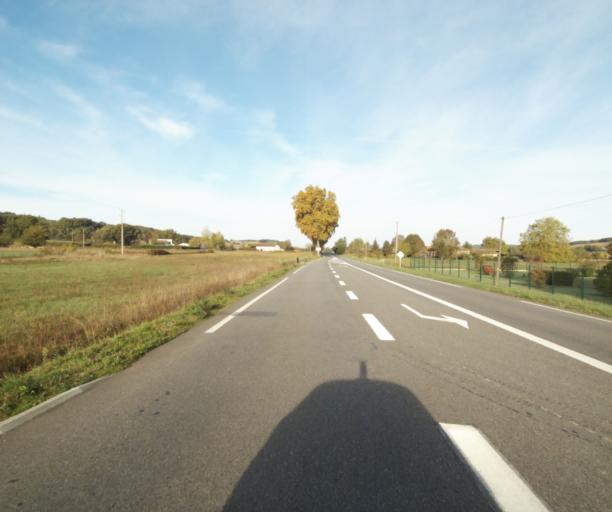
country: FR
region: Midi-Pyrenees
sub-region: Departement de la Haute-Garonne
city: Villemur-sur-Tarn
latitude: 43.9289
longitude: 1.5017
